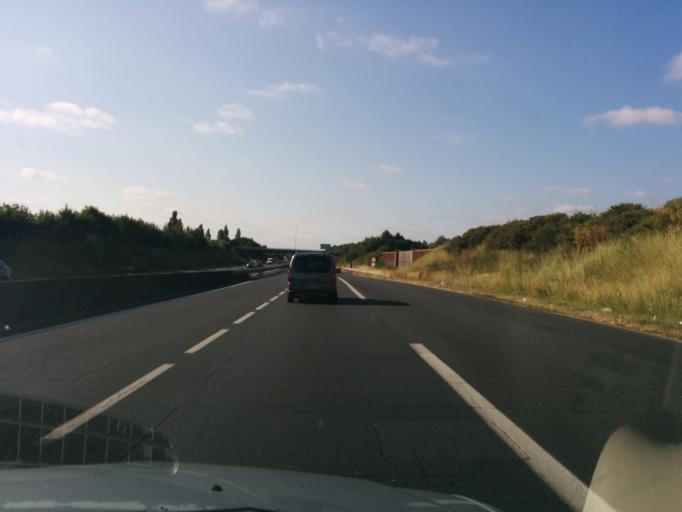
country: FR
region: Pays de la Loire
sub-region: Departement de la Loire-Atlantique
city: Sainte-Luce-sur-Loire
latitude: 47.2503
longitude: -1.4762
